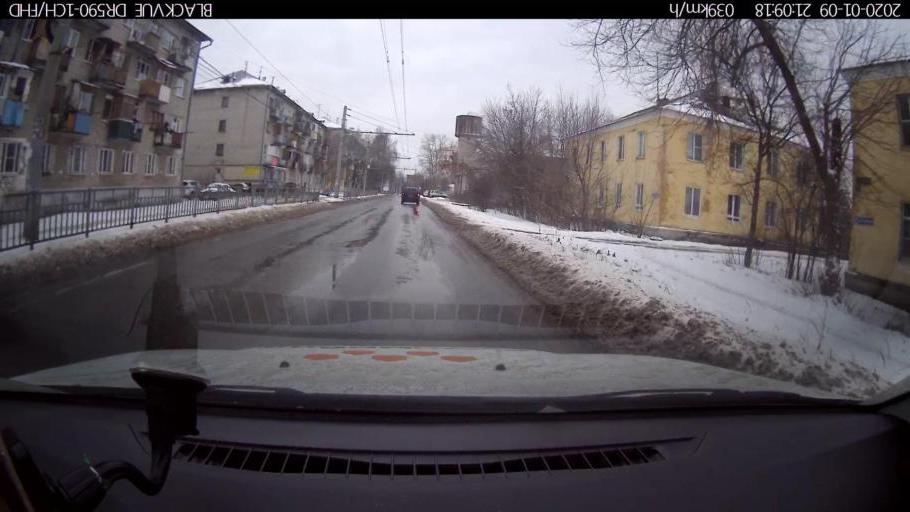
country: RU
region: Nizjnij Novgorod
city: Gorbatovka
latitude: 56.2912
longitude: 43.8578
